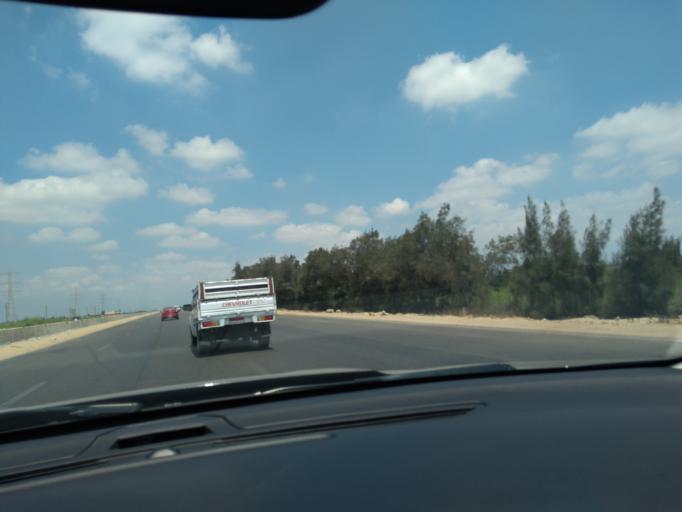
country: EG
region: Muhafazat Bur Sa`id
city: Port Said
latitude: 30.9786
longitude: 32.3080
